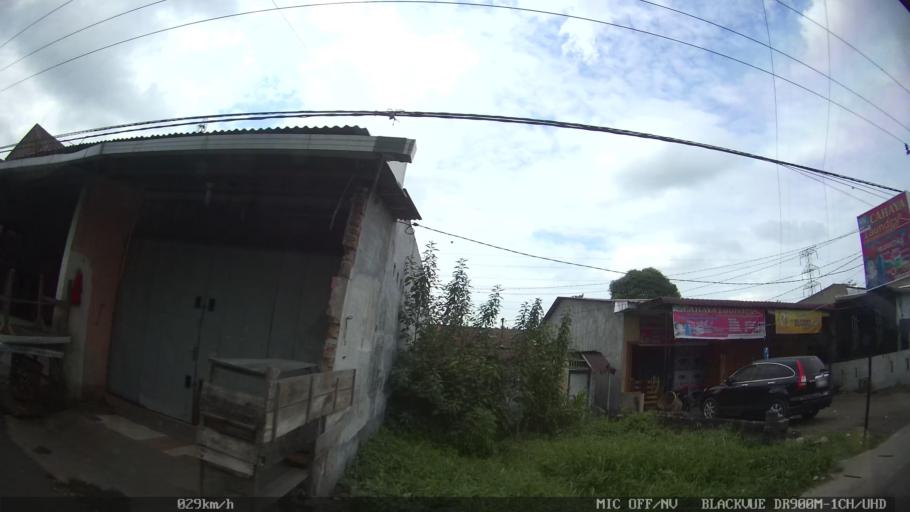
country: ID
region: North Sumatra
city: Sunggal
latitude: 3.6184
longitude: 98.6156
